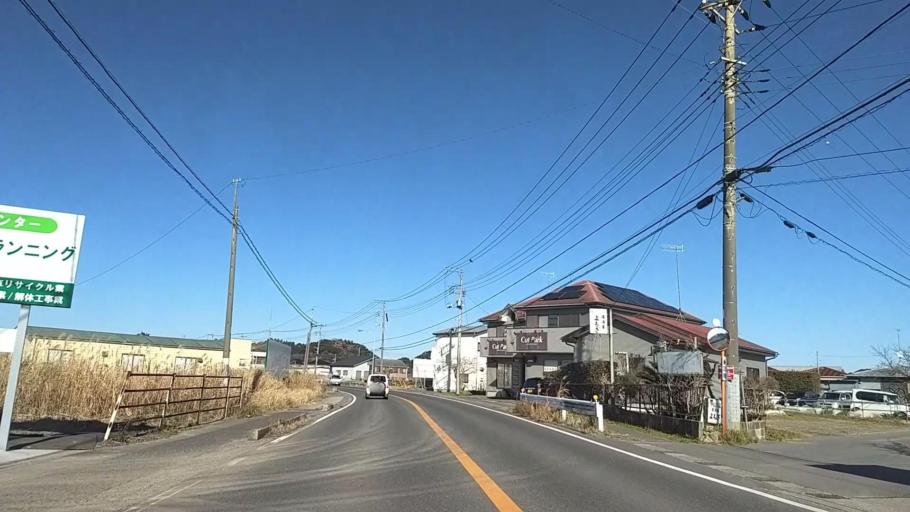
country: JP
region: Chiba
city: Ohara
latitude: 35.3045
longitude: 140.4005
